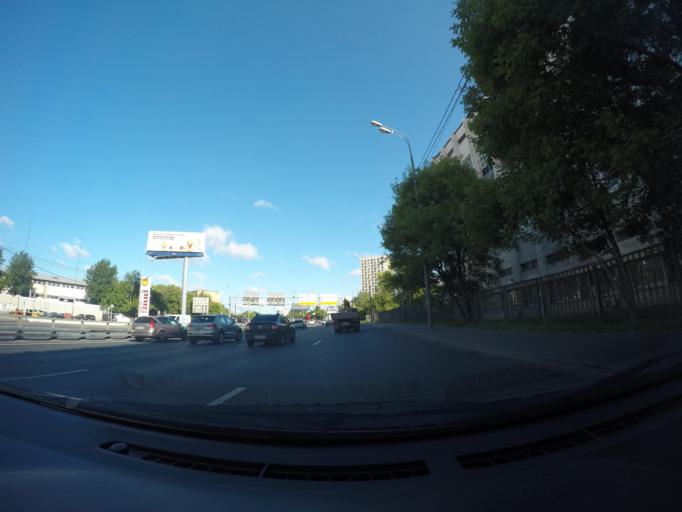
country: RU
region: Moscow
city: Sokol'niki
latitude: 55.7919
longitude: 37.6553
